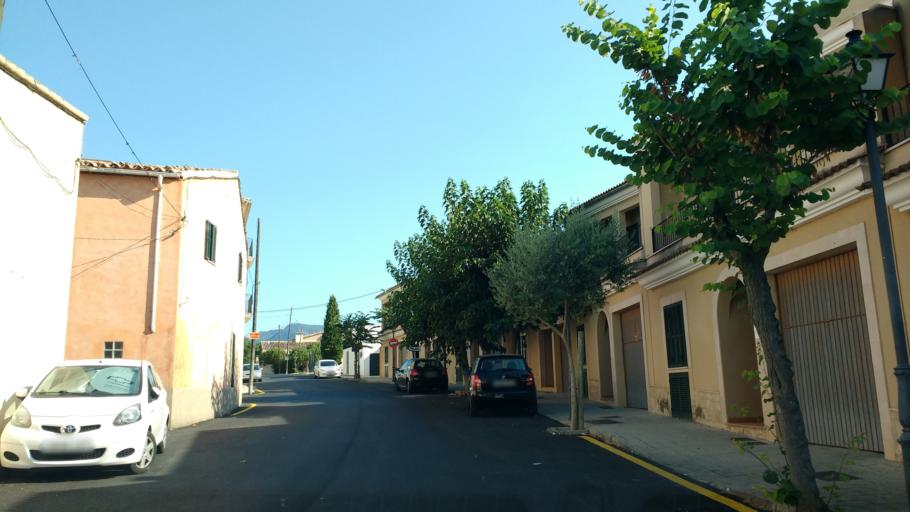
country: ES
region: Balearic Islands
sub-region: Illes Balears
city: Consell
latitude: 39.6707
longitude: 2.8133
